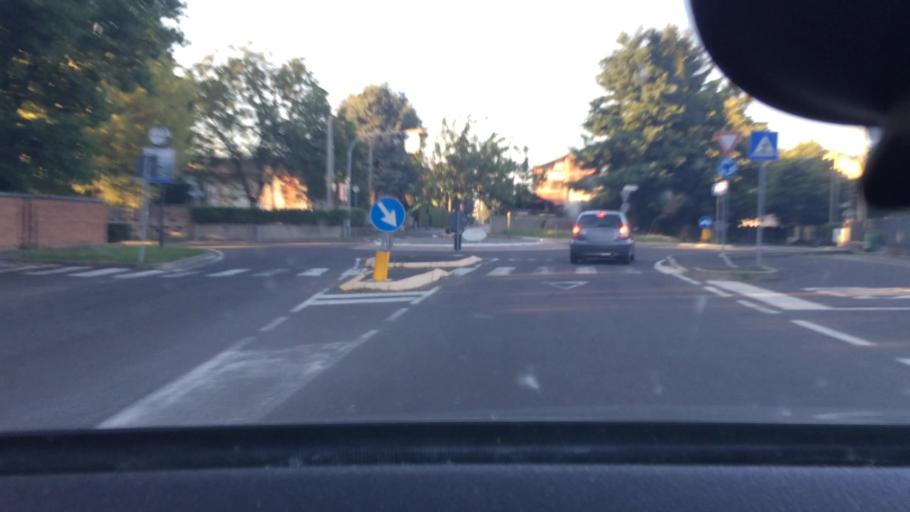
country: IT
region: Lombardy
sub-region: Provincia di Varese
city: Gerenzano
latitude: 45.6408
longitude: 8.9929
